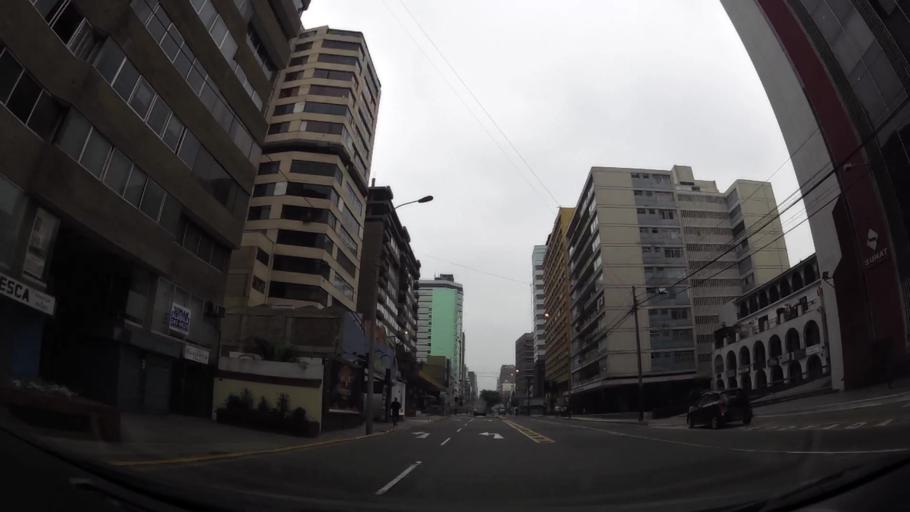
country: PE
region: Lima
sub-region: Lima
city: San Isidro
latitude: -12.1242
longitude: -77.0312
